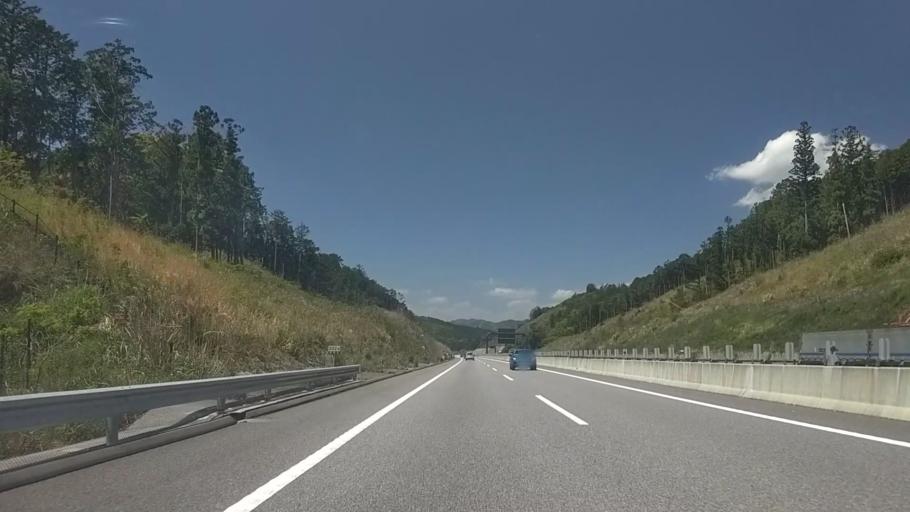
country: JP
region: Aichi
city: Shinshiro
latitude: 34.9029
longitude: 137.6175
